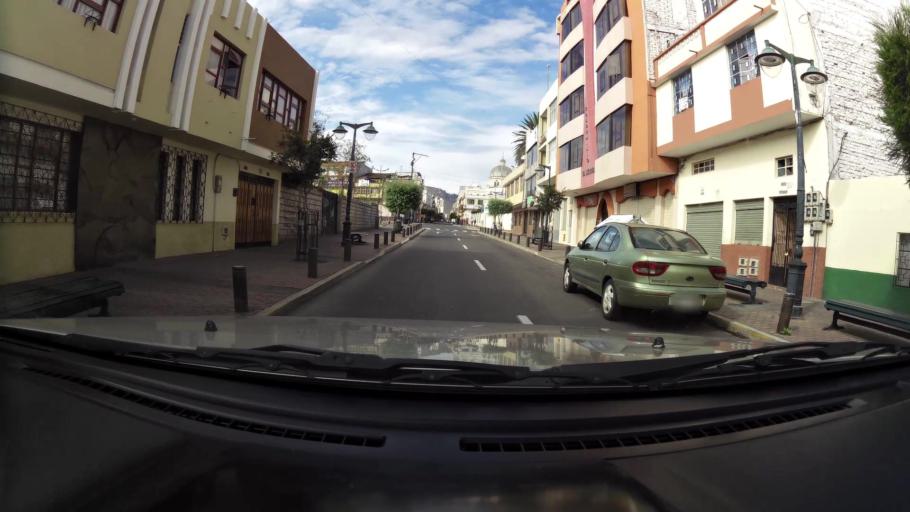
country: EC
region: Tungurahua
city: Ambato
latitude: -1.2355
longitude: -78.6265
